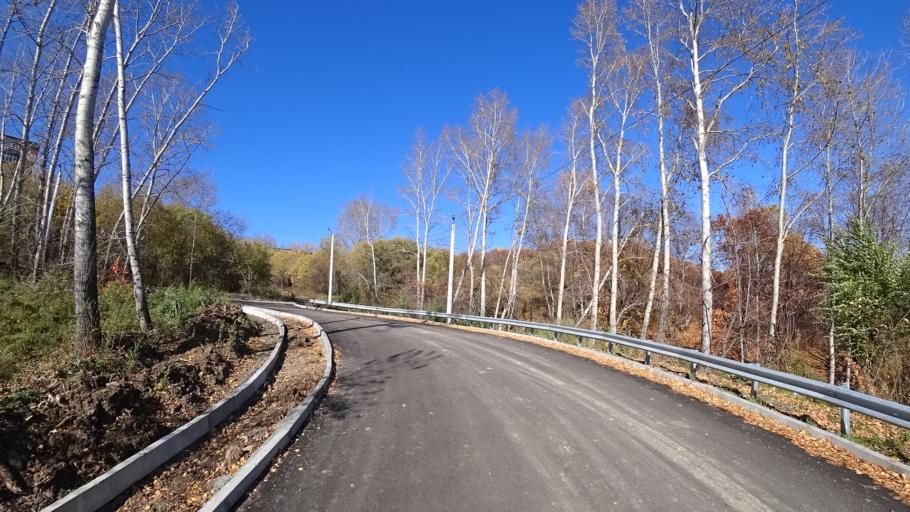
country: RU
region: Khabarovsk Krai
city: Amursk
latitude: 50.2164
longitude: 136.9074
